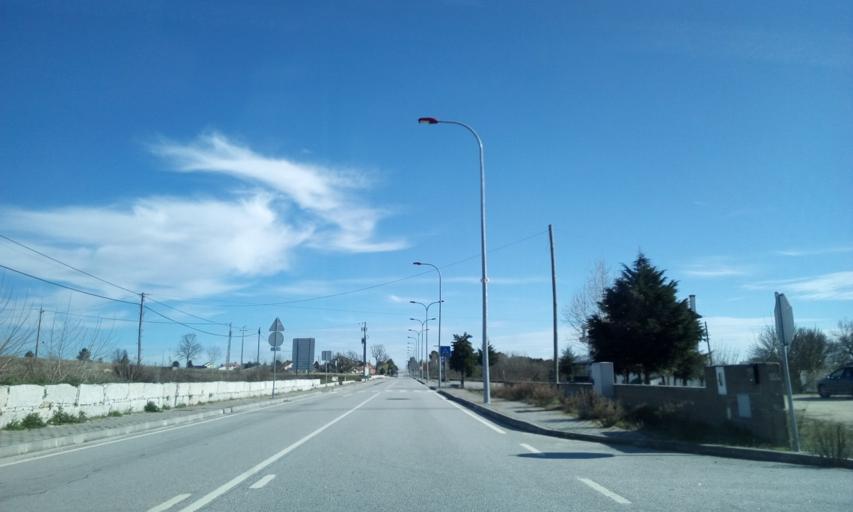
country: PT
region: Guarda
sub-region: Pinhel
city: Pinhel
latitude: 40.6025
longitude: -7.0012
